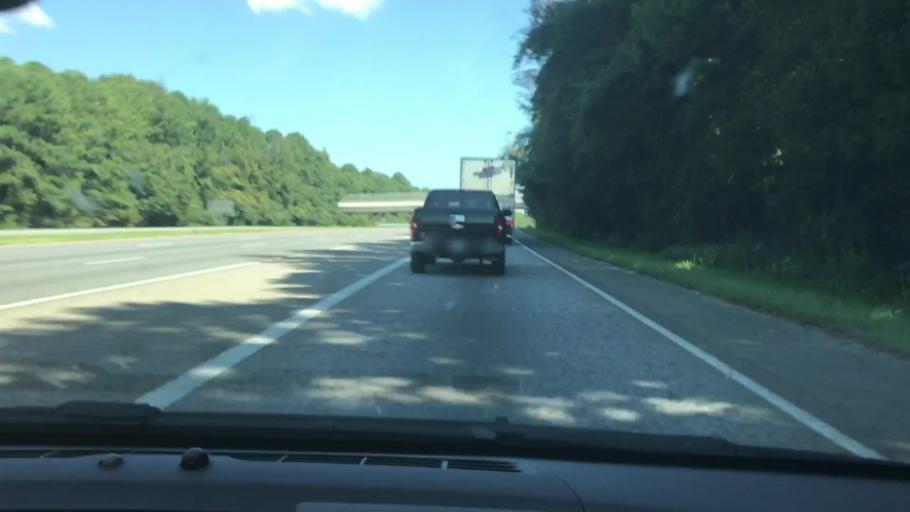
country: US
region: Alabama
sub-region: Russell County
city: Phenix City
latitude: 32.5537
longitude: -84.9621
